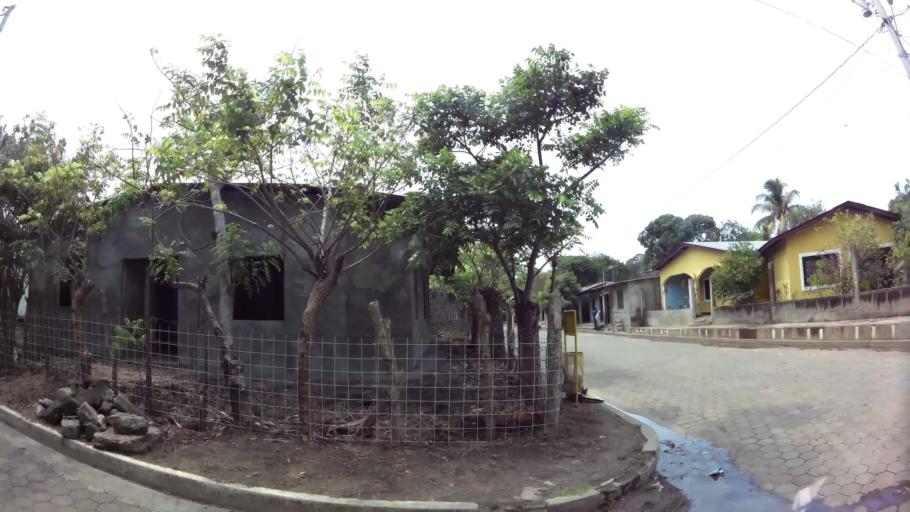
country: NI
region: Granada
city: Diria
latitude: 11.8856
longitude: -86.0530
